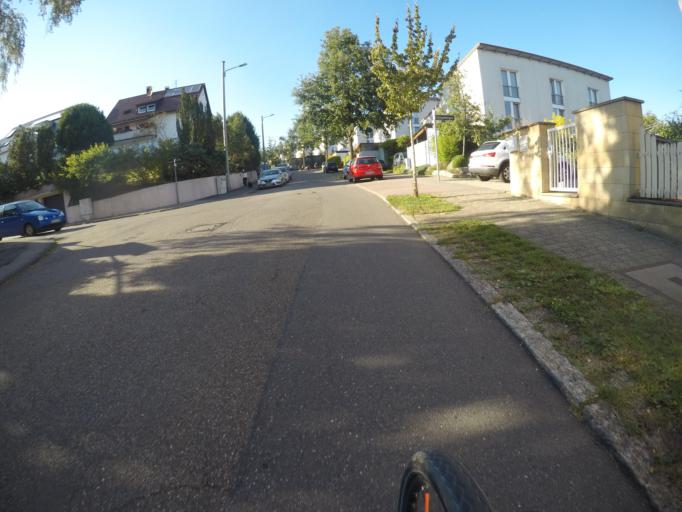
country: DE
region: Baden-Wuerttemberg
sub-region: Regierungsbezirk Stuttgart
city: Stuttgart Feuerbach
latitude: 48.8144
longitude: 9.1539
